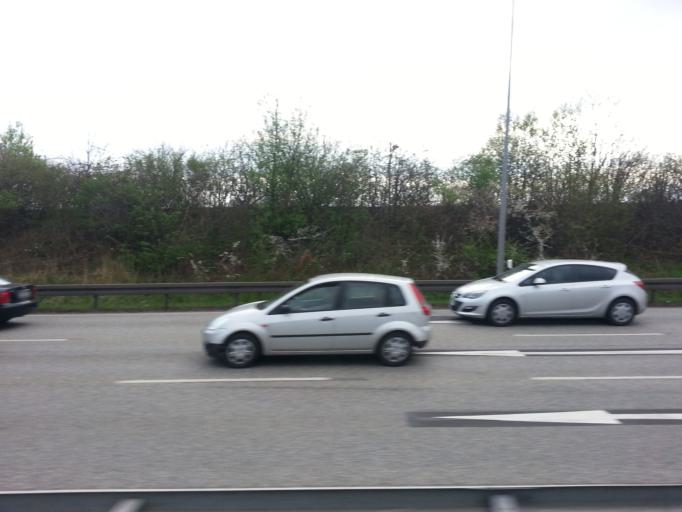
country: DE
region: Mecklenburg-Vorpommern
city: Lambrechtshagen
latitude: 54.1128
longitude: 12.0664
